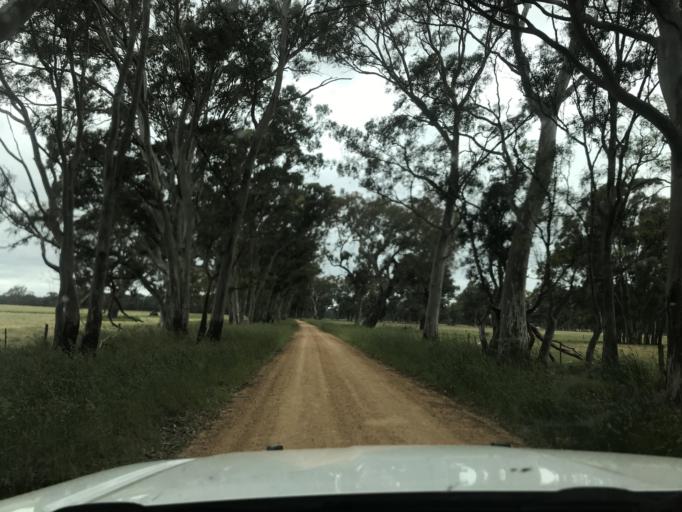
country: AU
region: South Australia
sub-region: Wattle Range
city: Penola
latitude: -37.2705
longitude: 140.9756
